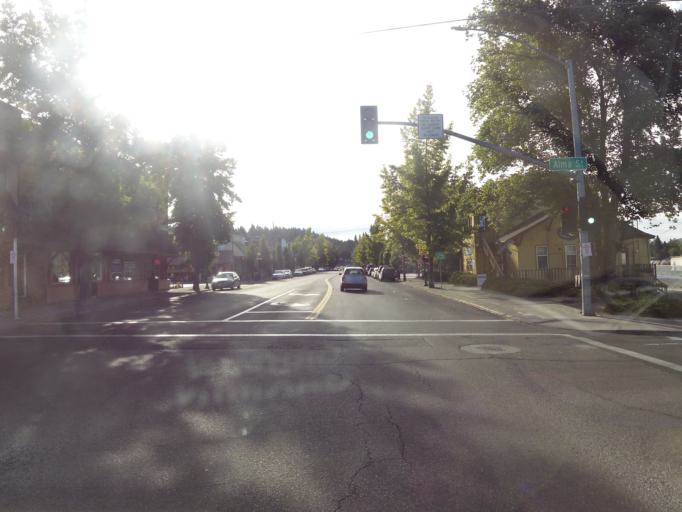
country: US
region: California
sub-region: Siskiyou County
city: Mount Shasta
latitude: 41.3151
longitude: -122.3149
